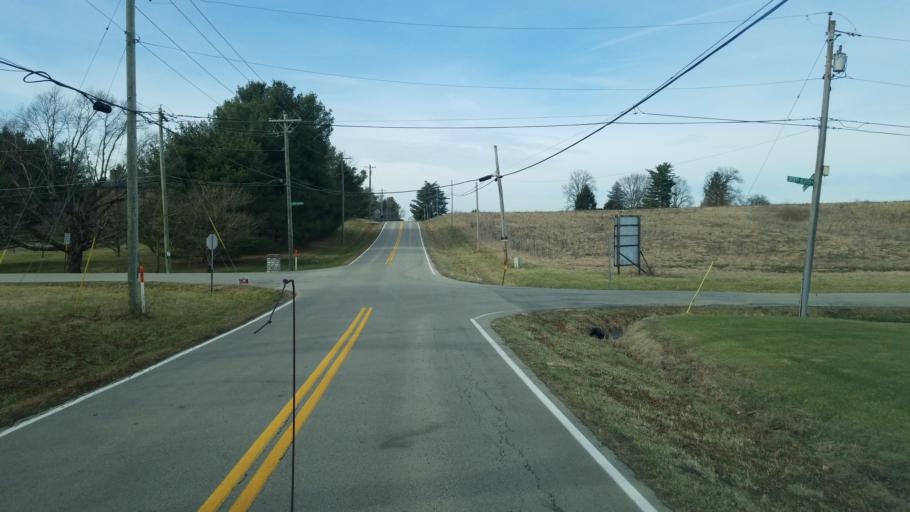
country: US
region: Ohio
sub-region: Warren County
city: Lebanon
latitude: 39.4301
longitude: -84.1587
